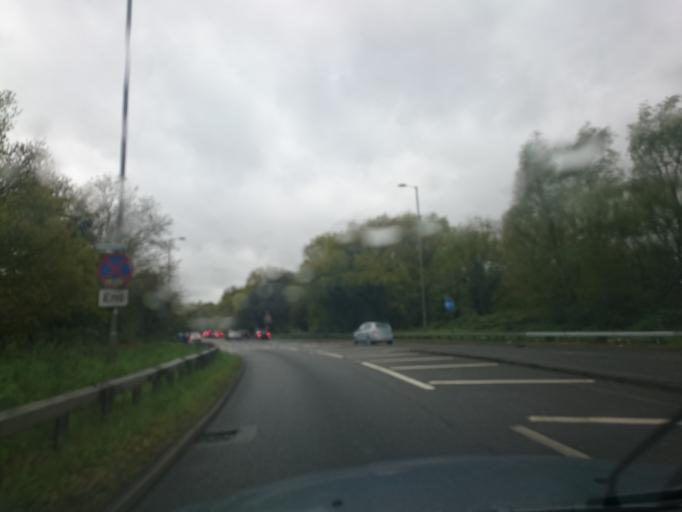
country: GB
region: England
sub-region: Surrey
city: Hale
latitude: 51.2199
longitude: -0.7763
